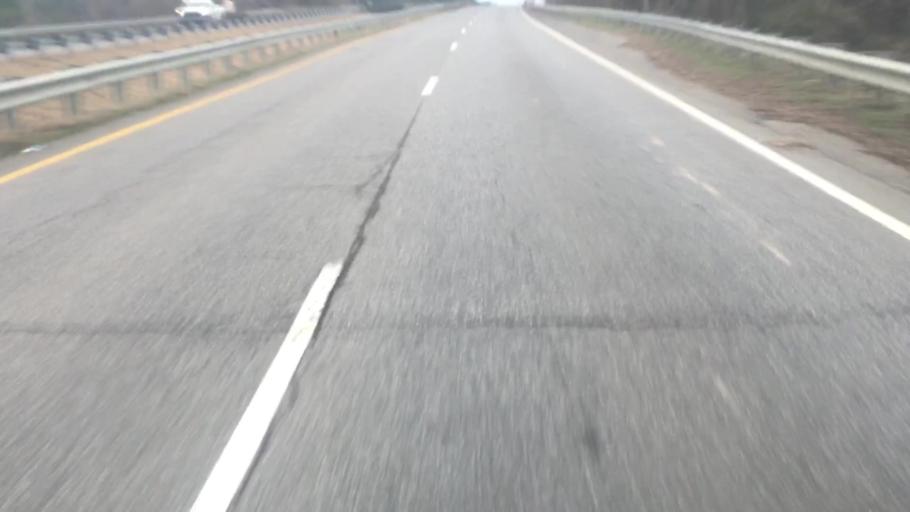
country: US
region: Alabama
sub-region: Jefferson County
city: Graysville
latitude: 33.6799
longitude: -86.9732
